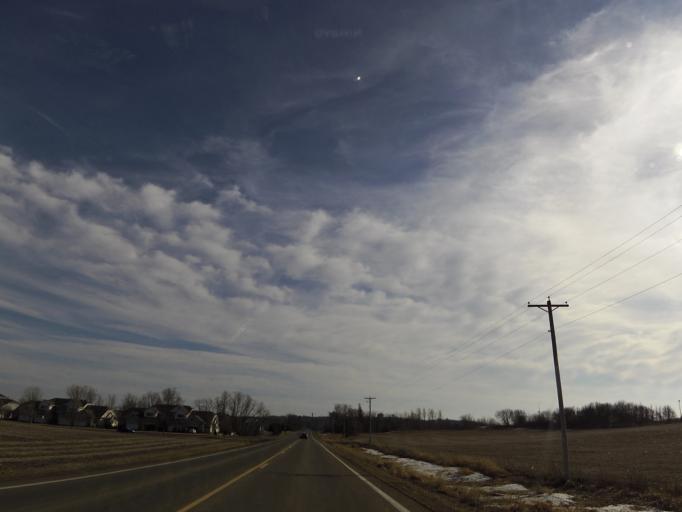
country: US
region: Minnesota
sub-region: Rice County
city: Northfield
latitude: 44.4797
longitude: -93.1807
